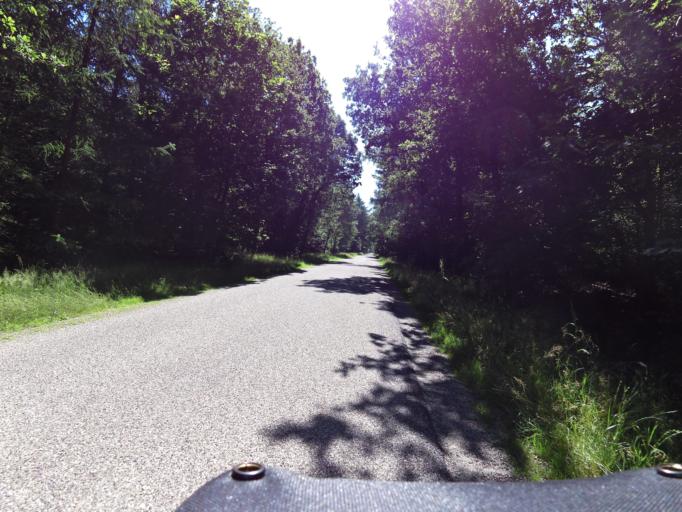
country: NL
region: Overijssel
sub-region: Gemeente Twenterand
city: Den Ham
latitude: 52.5404
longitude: 6.4856
